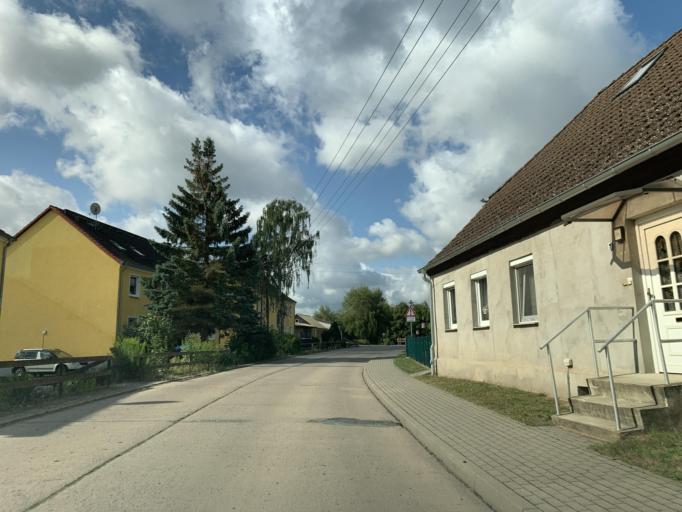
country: DE
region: Mecklenburg-Vorpommern
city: Carpin
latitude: 53.3754
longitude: 13.1808
